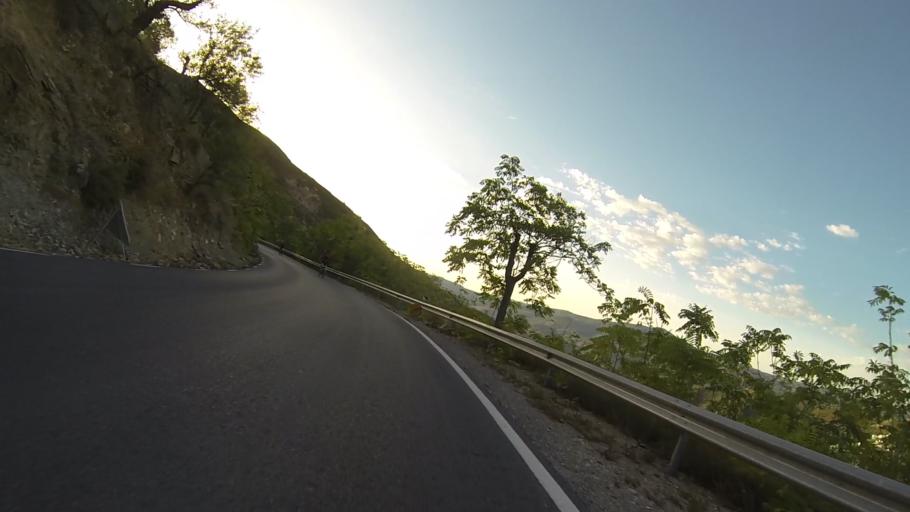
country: ES
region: Andalusia
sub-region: Provincia de Granada
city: Berchules
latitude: 36.9826
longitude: -3.1470
